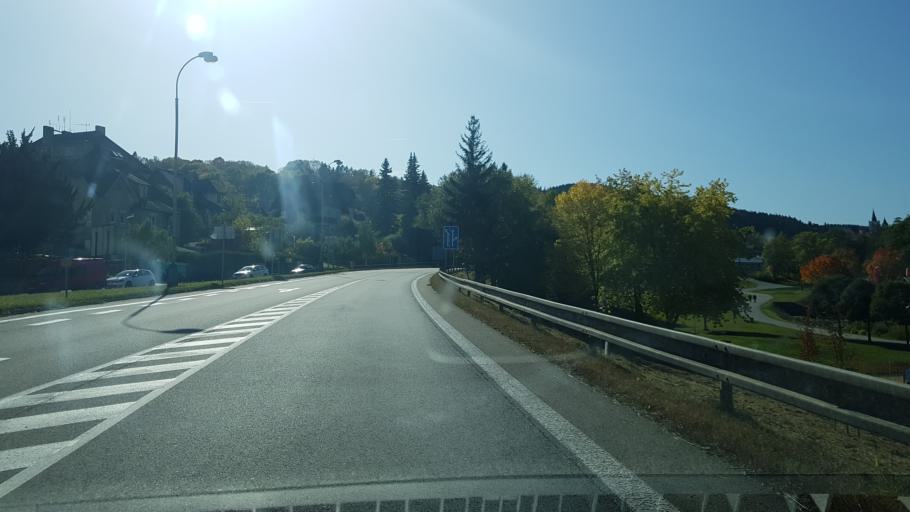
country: CZ
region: Jihocesky
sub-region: Okres Prachatice
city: Vimperk
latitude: 49.0557
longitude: 13.7853
